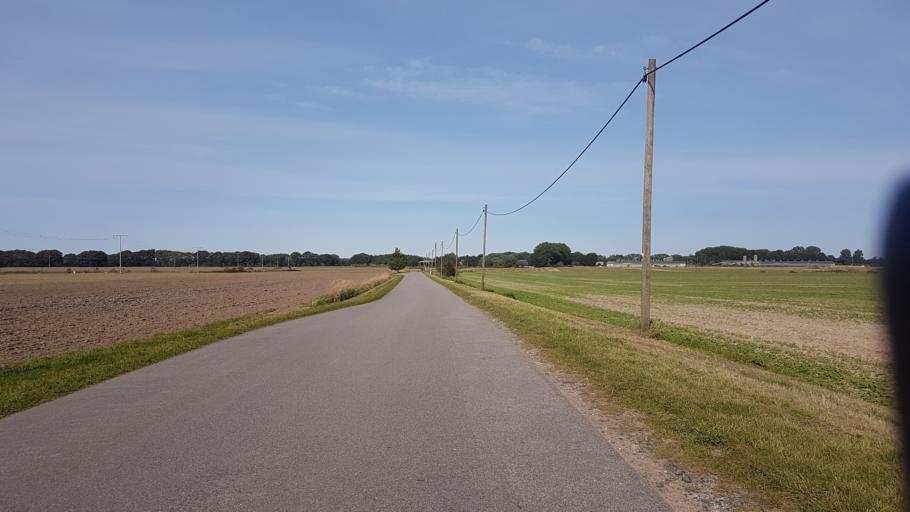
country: DE
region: Mecklenburg-Vorpommern
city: Gingst
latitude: 54.4283
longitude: 13.2234
